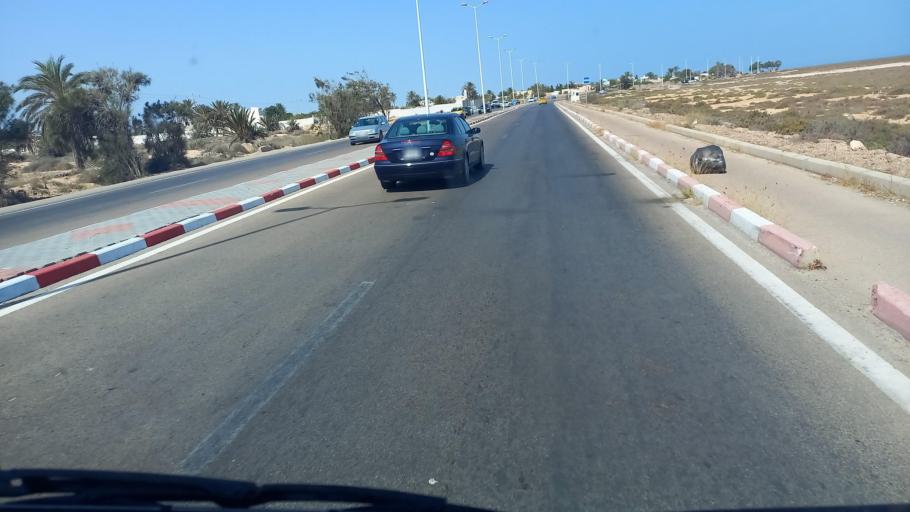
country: TN
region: Madanin
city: Midoun
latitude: 33.8694
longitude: 10.9404
